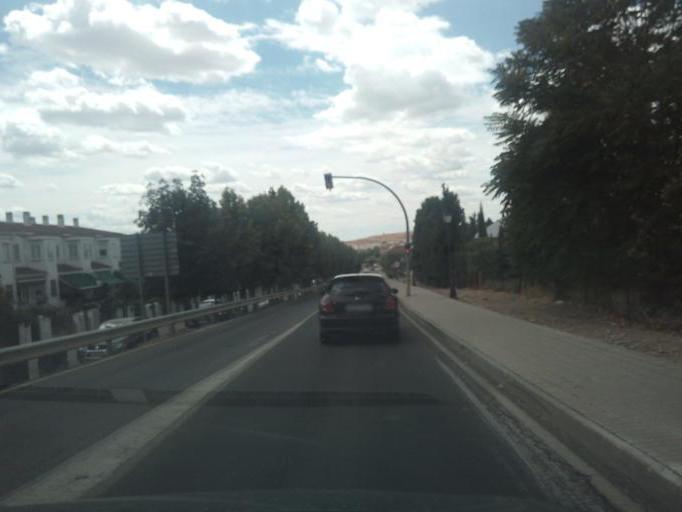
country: ES
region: Madrid
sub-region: Provincia de Madrid
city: Ajalvir
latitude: 40.5361
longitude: -3.4771
